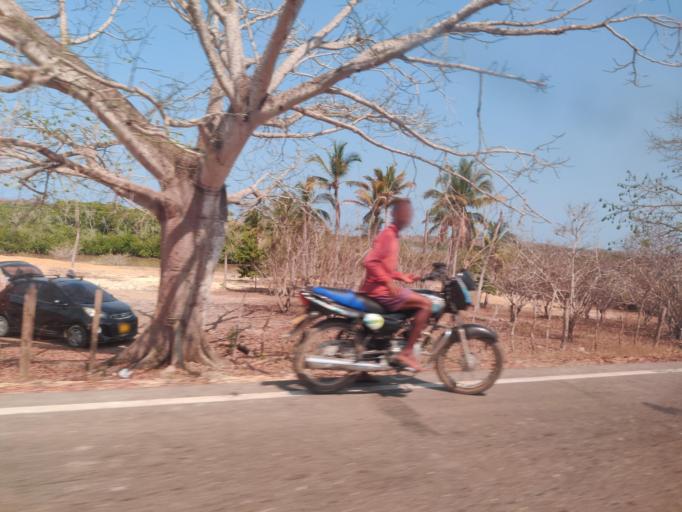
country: CO
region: Bolivar
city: Turbana
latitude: 10.1658
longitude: -75.6513
